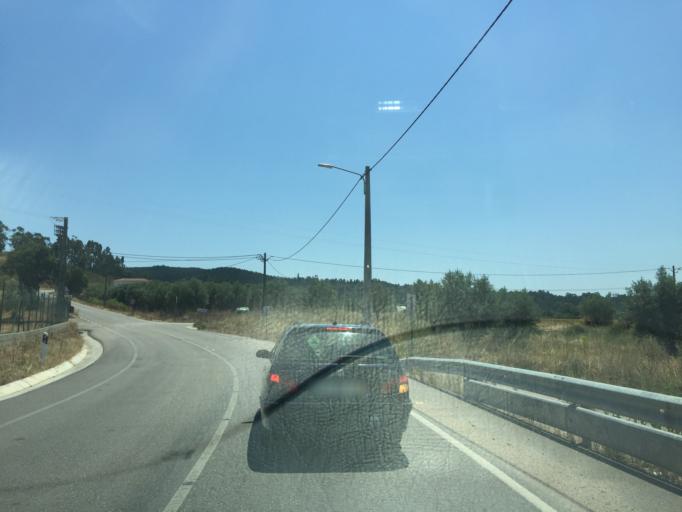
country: PT
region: Santarem
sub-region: Tomar
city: Tomar
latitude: 39.5918
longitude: -8.3598
